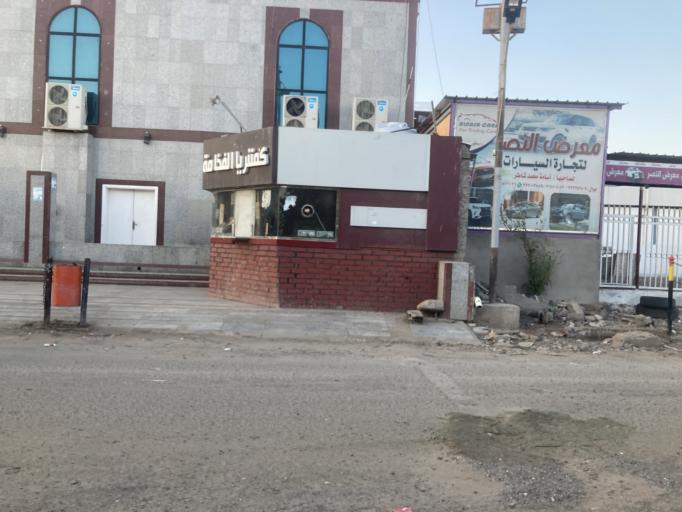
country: YE
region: Aden
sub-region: Ash Shaikh Outhman
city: Ash Shaykh `Uthman
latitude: 12.8620
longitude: 45.0155
